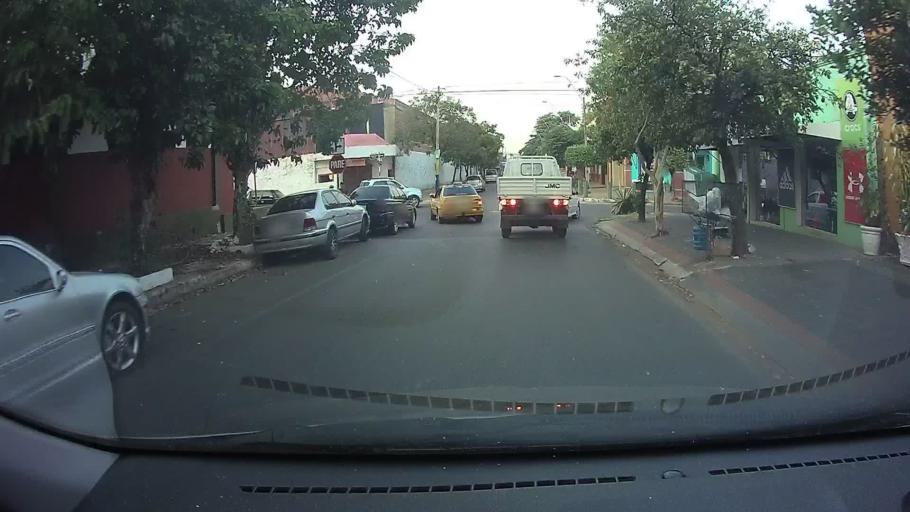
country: PY
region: Central
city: San Lorenzo
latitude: -25.2657
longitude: -57.4905
